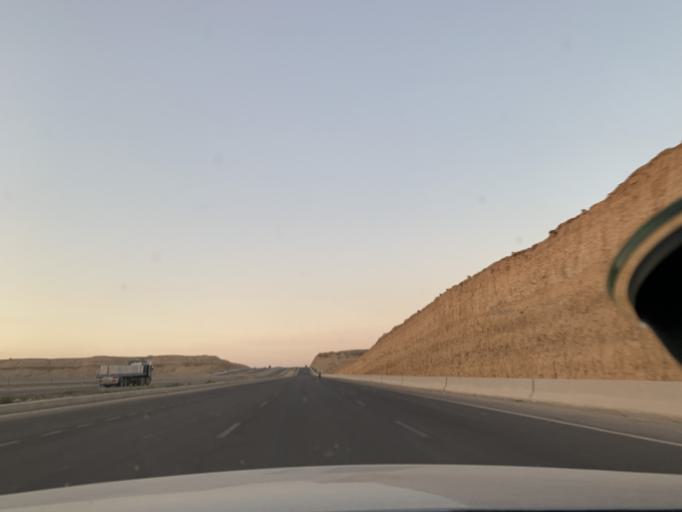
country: EG
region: Muhafazat al Qahirah
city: Halwan
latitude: 29.9442
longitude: 31.5340
